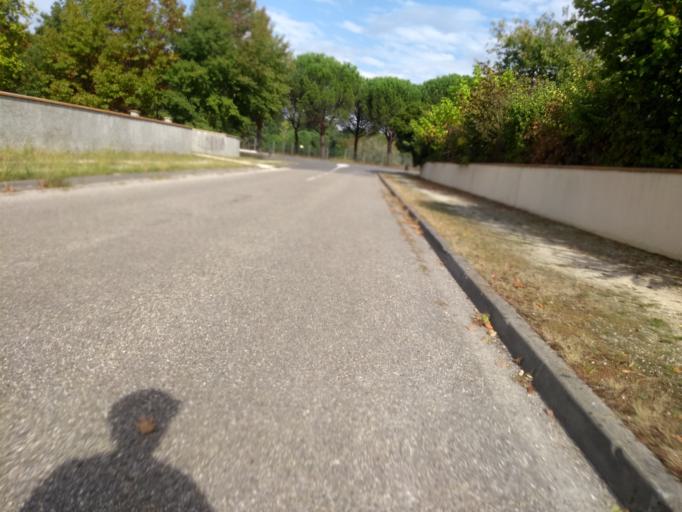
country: FR
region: Aquitaine
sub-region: Departement de la Gironde
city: Cestas
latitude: 44.7424
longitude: -0.6552
